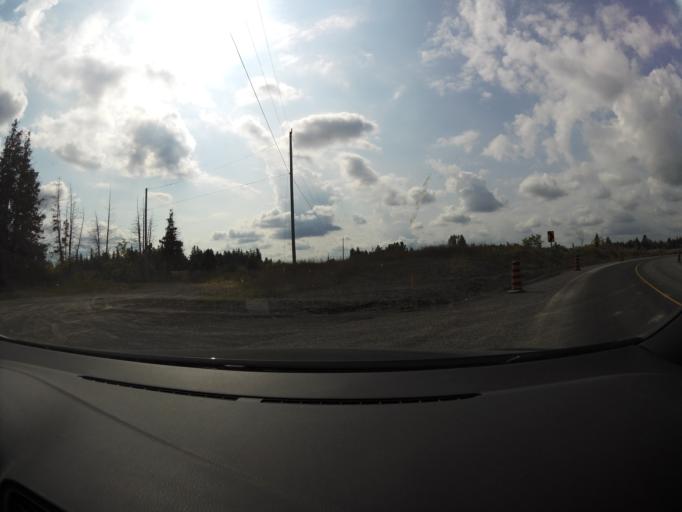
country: CA
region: Ontario
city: Arnprior
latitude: 45.3474
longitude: -76.2010
